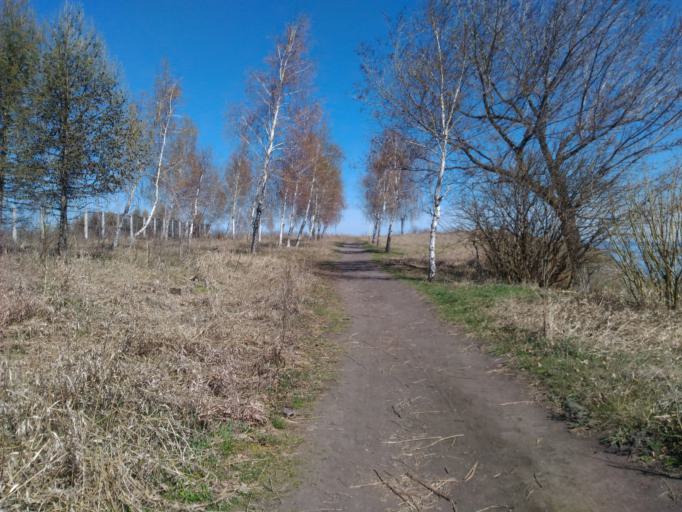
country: RU
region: Ulyanovsk
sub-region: Ulyanovskiy Rayon
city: Ulyanovsk
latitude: 54.3520
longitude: 48.3931
